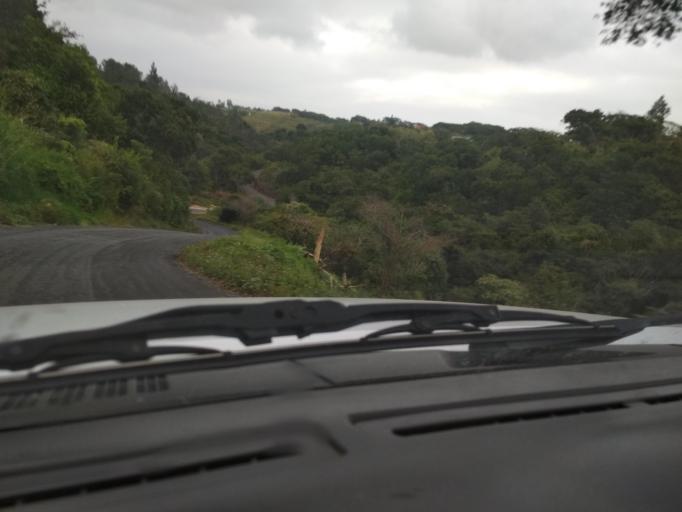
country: MX
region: Veracruz
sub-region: Emiliano Zapata
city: Dos Rios
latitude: 19.5243
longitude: -96.7971
